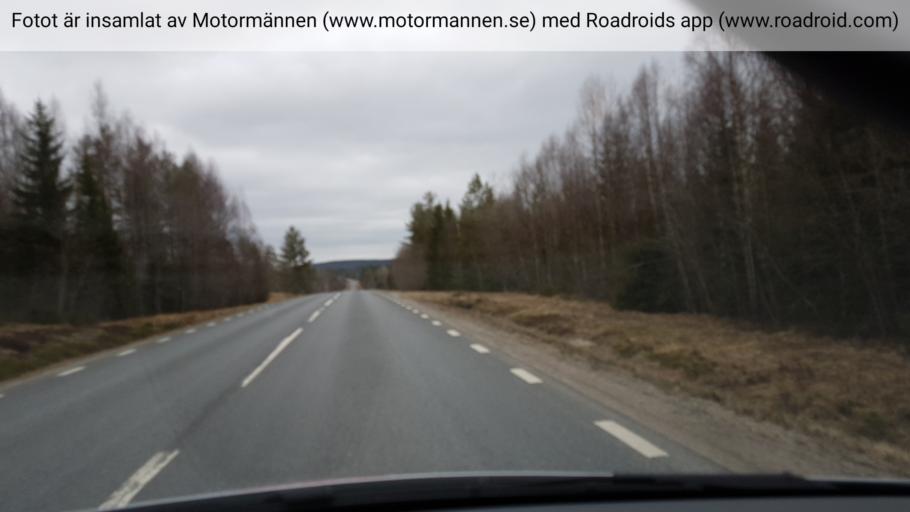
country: SE
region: Vaesternorrland
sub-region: OErnskoeldsviks Kommun
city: Ornskoldsvik
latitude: 63.5792
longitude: 18.5510
